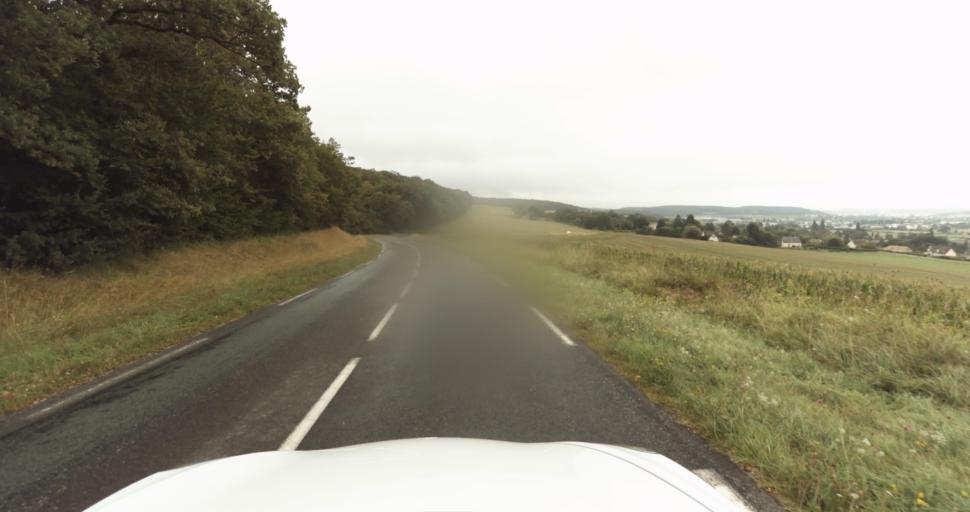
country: FR
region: Haute-Normandie
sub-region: Departement de l'Eure
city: Normanville
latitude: 49.0753
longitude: 1.1719
